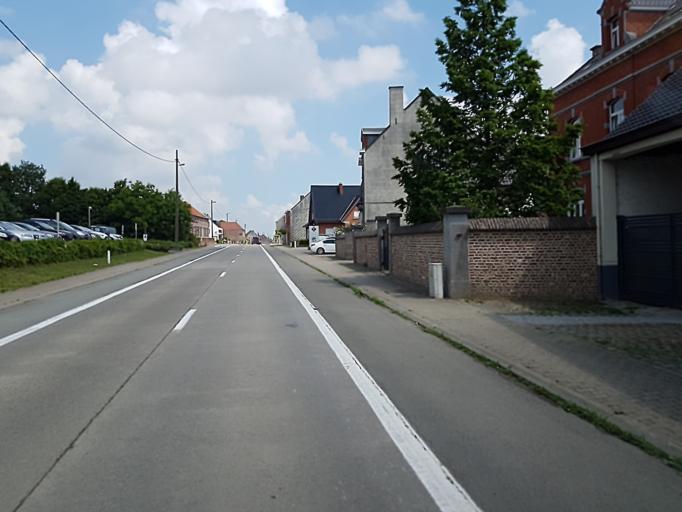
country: BE
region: Flanders
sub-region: Provincie Vlaams-Brabant
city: Gooik
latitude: 50.7432
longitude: 4.0965
